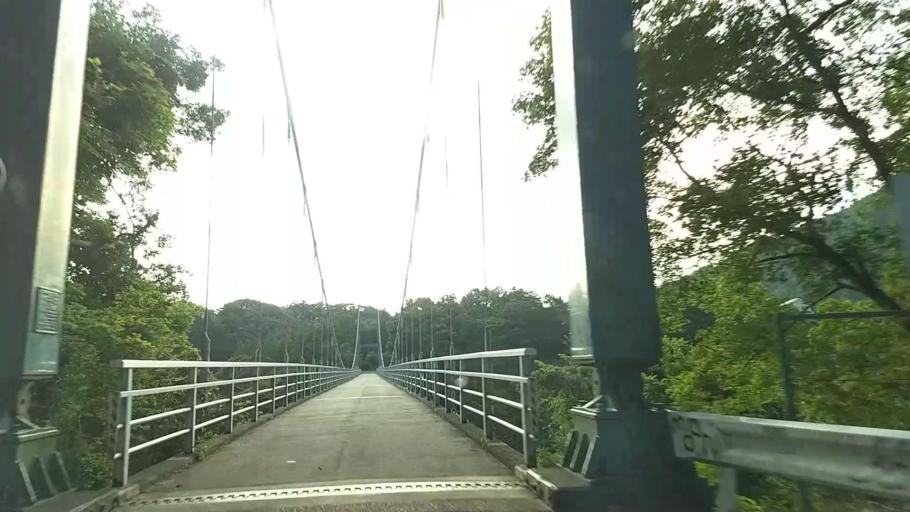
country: JP
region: Tokyo
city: Hachioji
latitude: 35.5983
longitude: 139.2436
